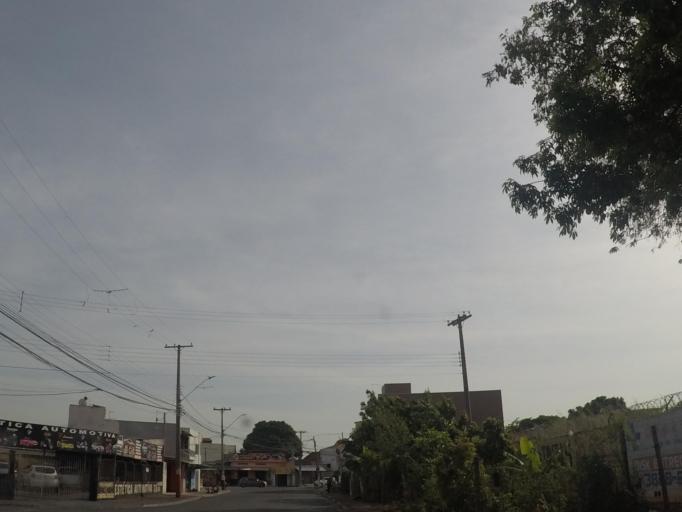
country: BR
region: Sao Paulo
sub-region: Hortolandia
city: Hortolandia
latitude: -22.8548
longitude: -47.1933
